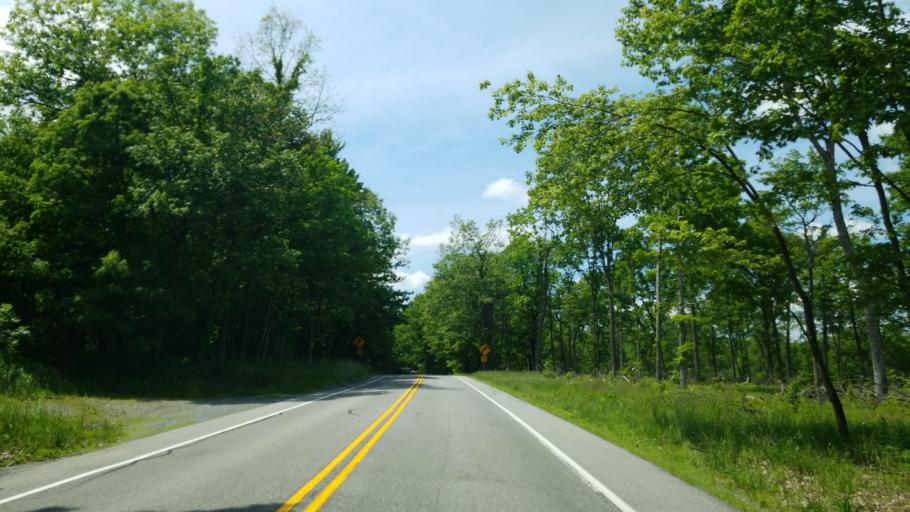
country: US
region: Pennsylvania
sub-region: Blair County
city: Tipton
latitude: 40.7059
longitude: -78.3114
